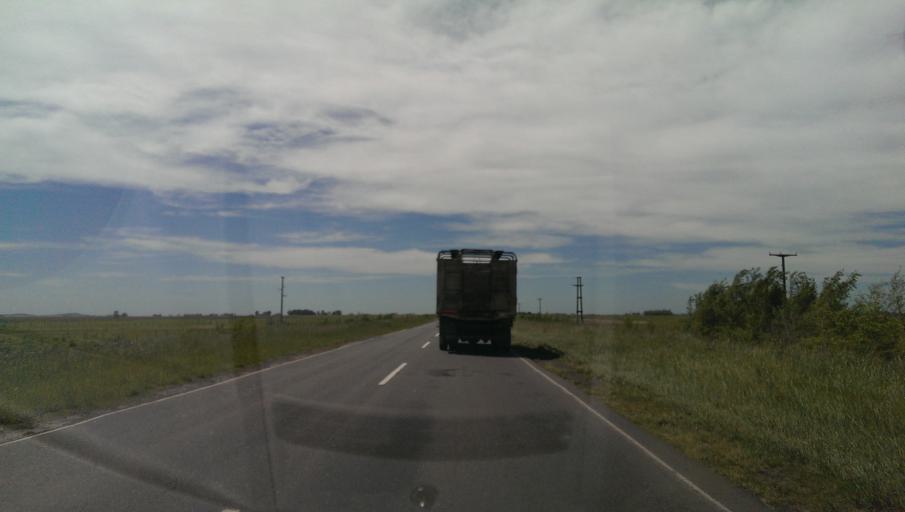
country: AR
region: Buenos Aires
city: Olavarria
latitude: -37.0624
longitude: -60.4613
